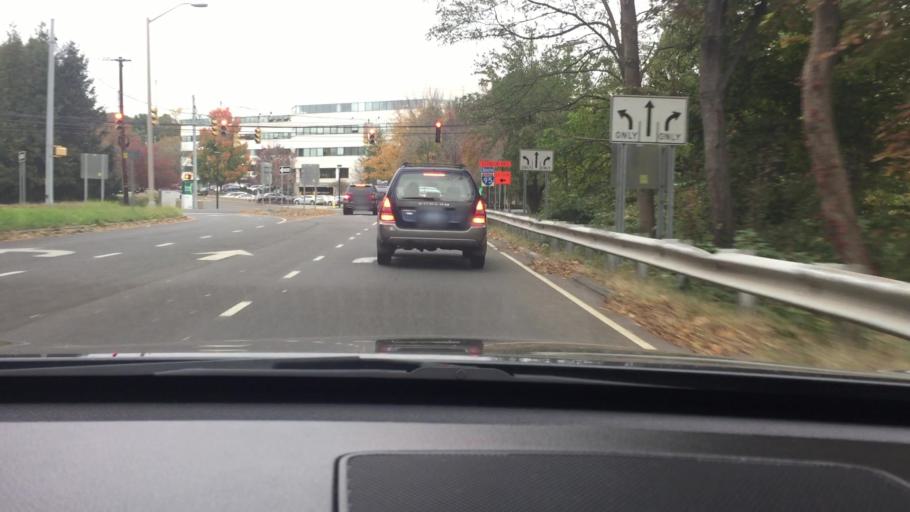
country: US
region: Connecticut
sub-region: Fairfield County
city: Darien
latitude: 41.0910
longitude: -73.4539
